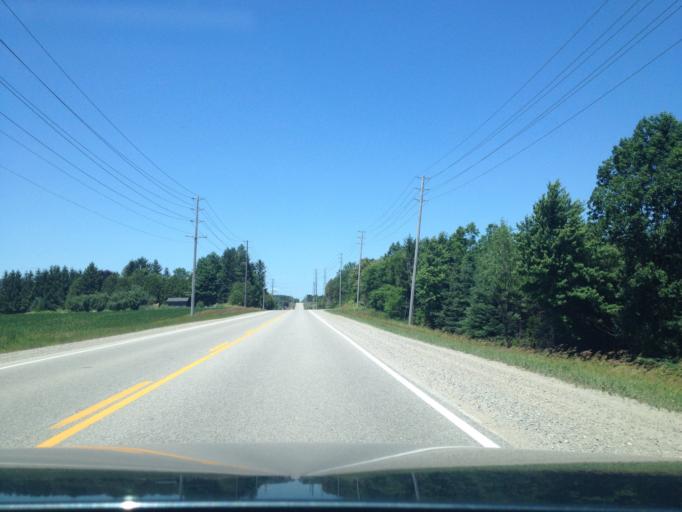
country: CA
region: Ontario
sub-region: Wellington County
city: Guelph
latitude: 43.6974
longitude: -80.3290
